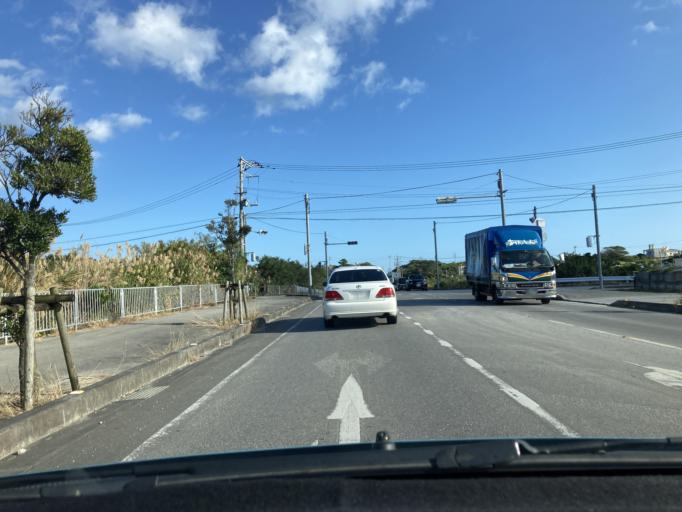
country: JP
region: Okinawa
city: Gushikawa
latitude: 26.3862
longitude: 127.8440
